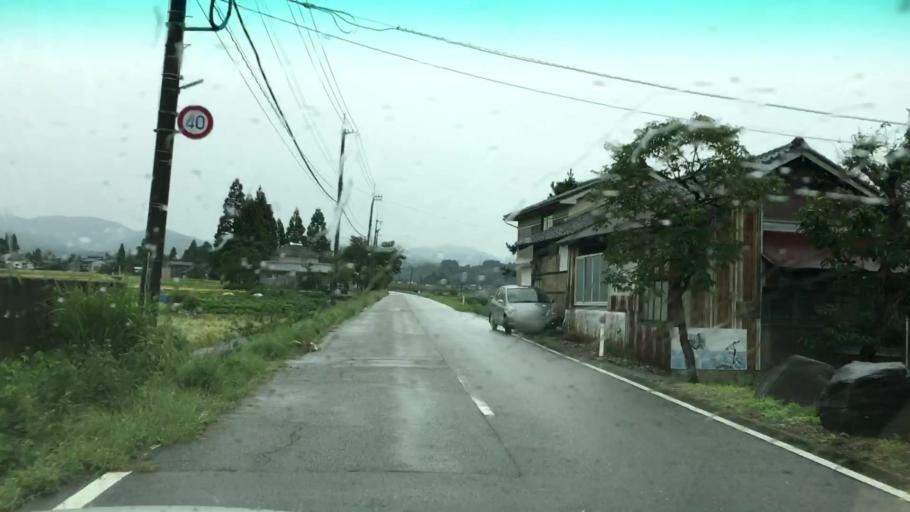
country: JP
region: Toyama
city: Kamiichi
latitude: 36.6192
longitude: 137.3227
